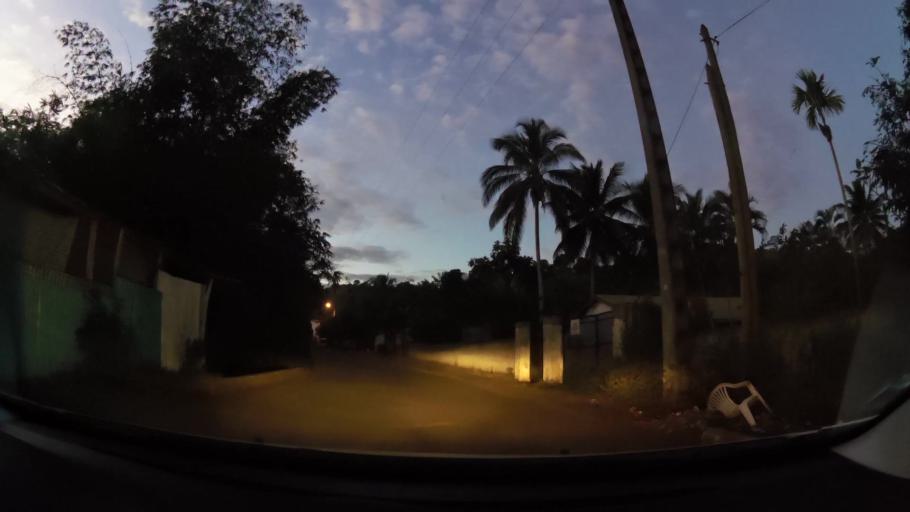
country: YT
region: Bandraboua
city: Bandraboua
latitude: -12.7219
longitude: 45.1190
